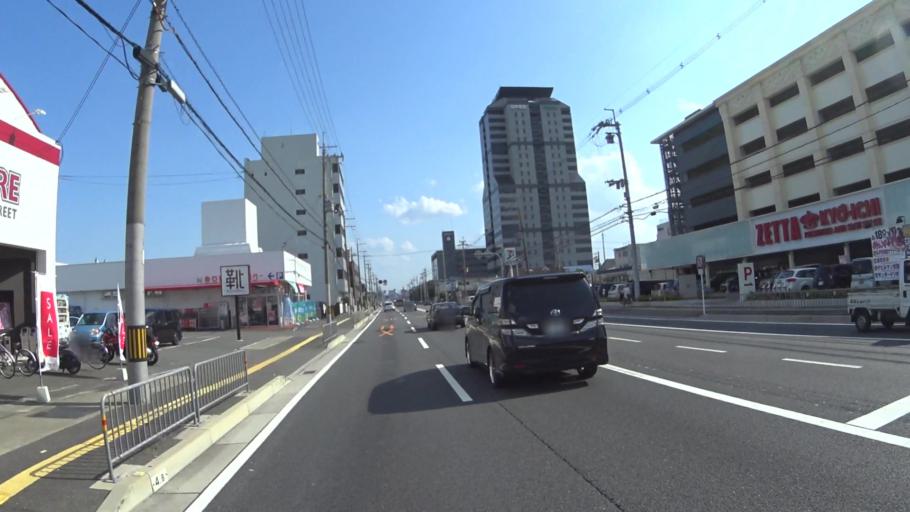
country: JP
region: Kyoto
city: Muko
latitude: 34.9538
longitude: 135.7168
